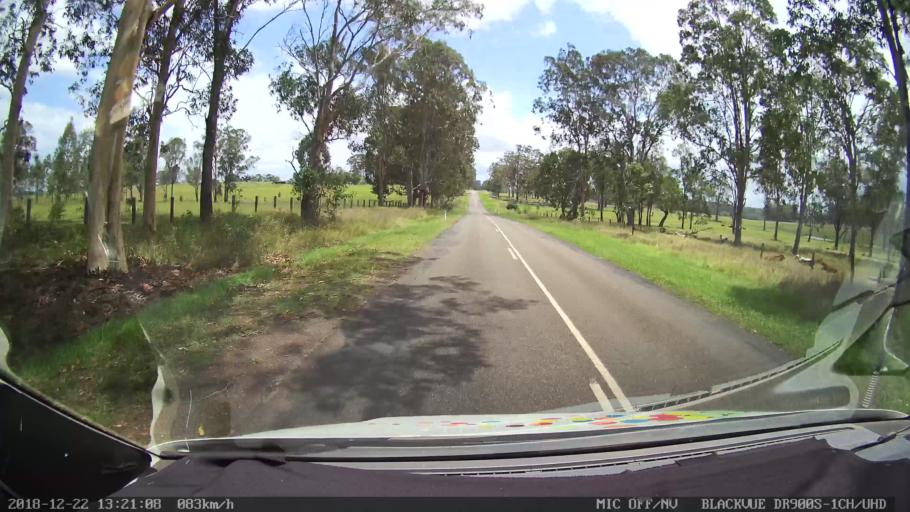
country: AU
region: New South Wales
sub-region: Clarence Valley
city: Coutts Crossing
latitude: -29.7738
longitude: 152.9231
